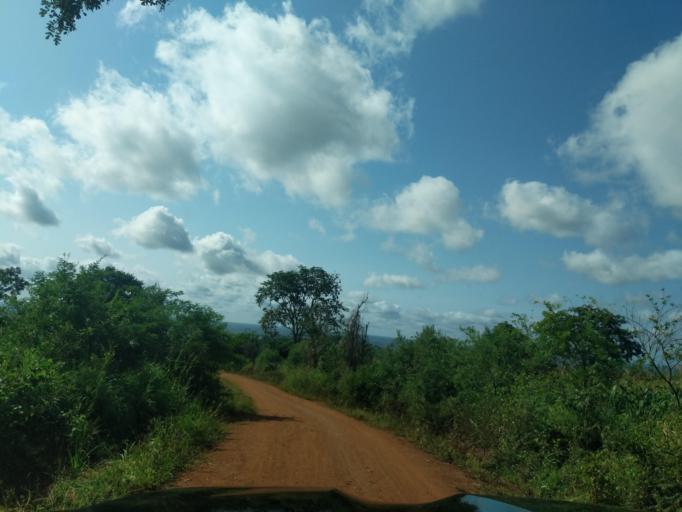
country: TZ
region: Tanga
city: Muheza
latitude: -5.4201
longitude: 38.6298
